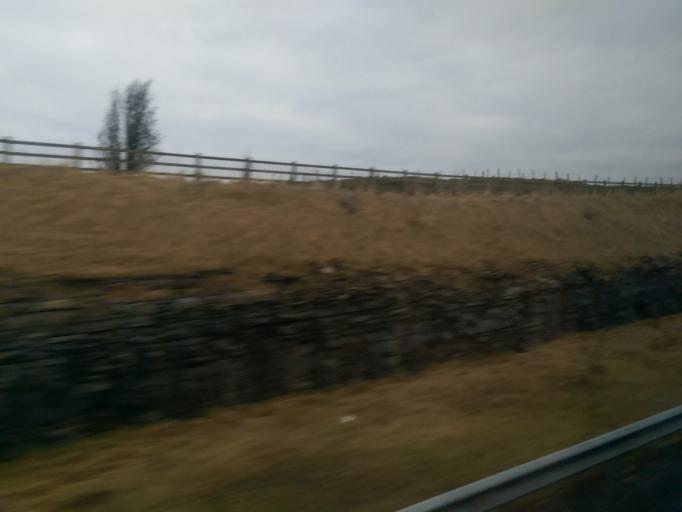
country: IE
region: Connaught
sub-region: County Galway
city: Loughrea
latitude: 53.2814
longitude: -8.5145
